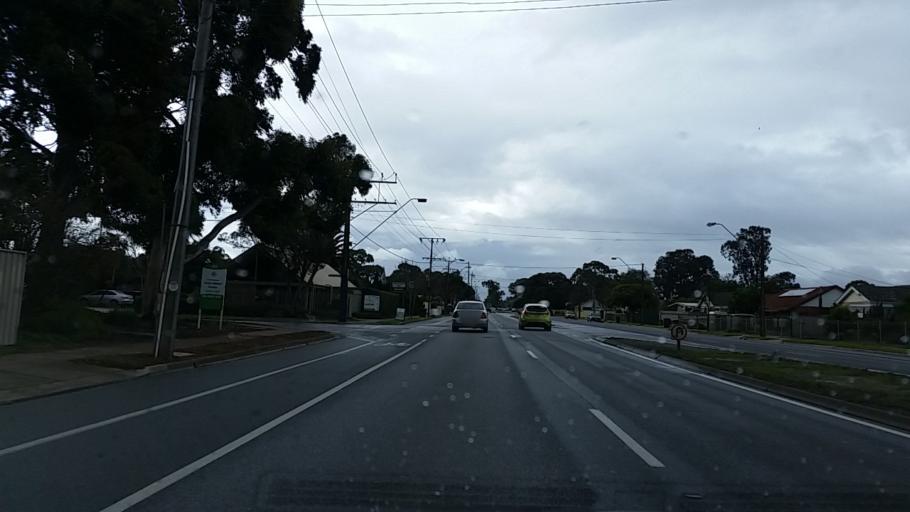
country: AU
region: South Australia
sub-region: Salisbury
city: Salisbury
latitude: -34.7901
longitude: 138.6165
